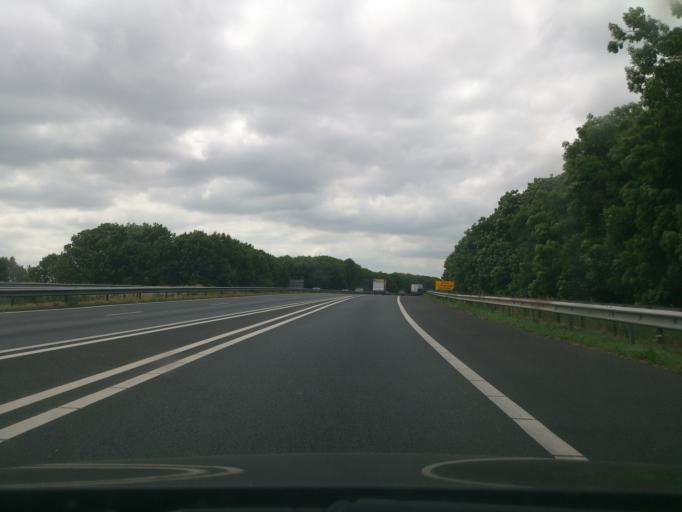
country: NL
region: Gelderland
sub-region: Gemeente Wijchen
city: Bergharen
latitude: 51.8080
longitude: 5.6772
